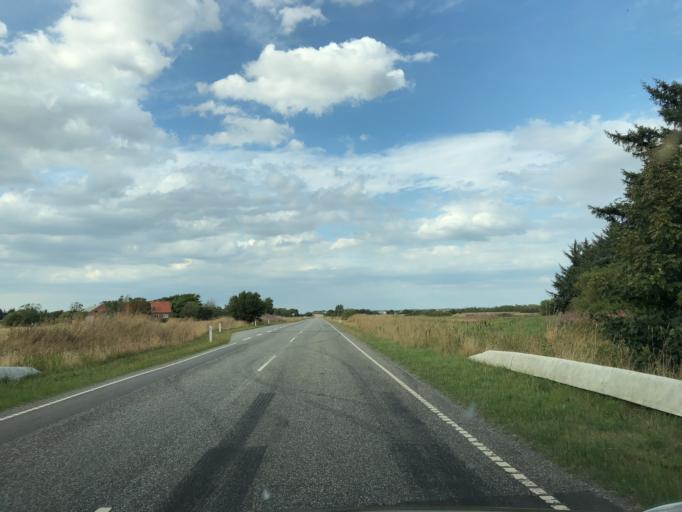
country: DK
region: Central Jutland
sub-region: Struer Kommune
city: Struer
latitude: 56.3932
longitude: 8.4576
